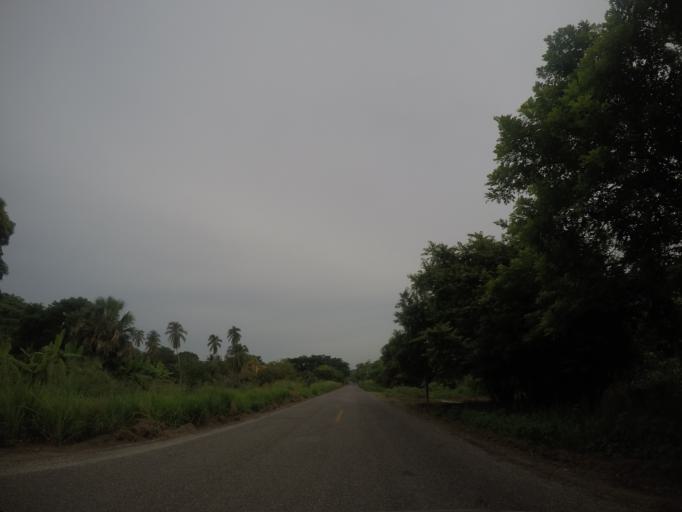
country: MX
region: Oaxaca
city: San Pedro Mixtepec
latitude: 15.9357
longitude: -97.1553
